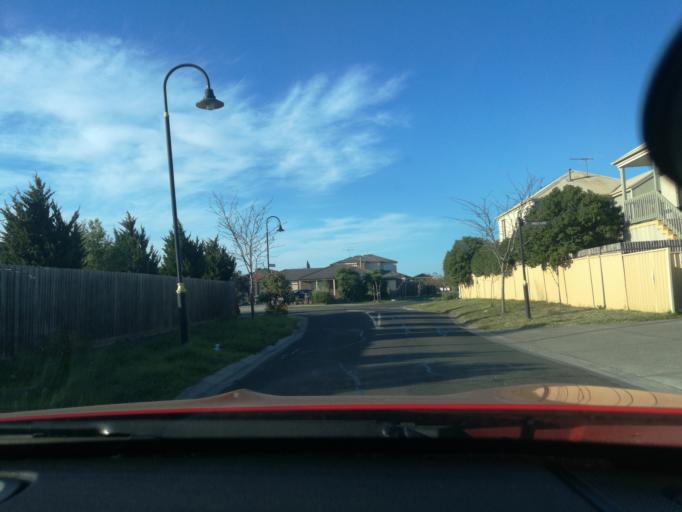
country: AU
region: Victoria
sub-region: Wyndham
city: Williams Landing
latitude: -37.8786
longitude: 144.7458
